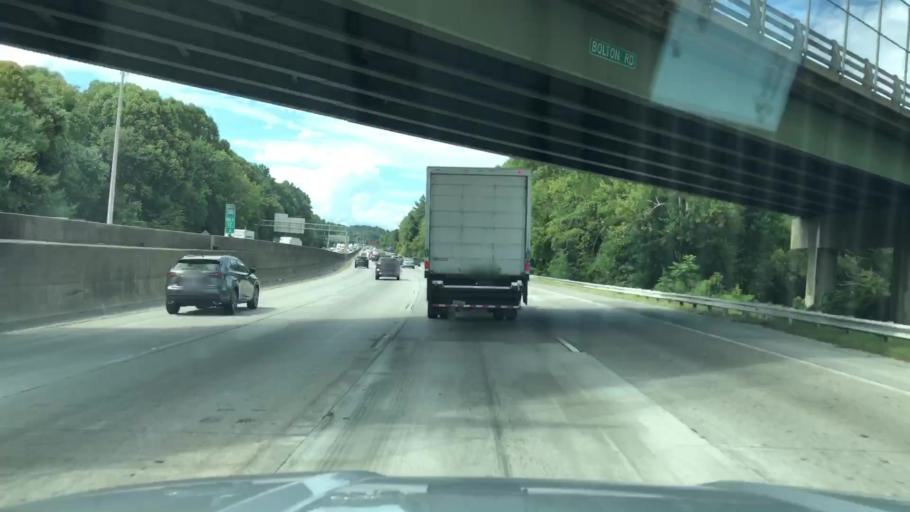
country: US
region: Georgia
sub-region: Cobb County
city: Vinings
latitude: 33.7995
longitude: -84.4883
